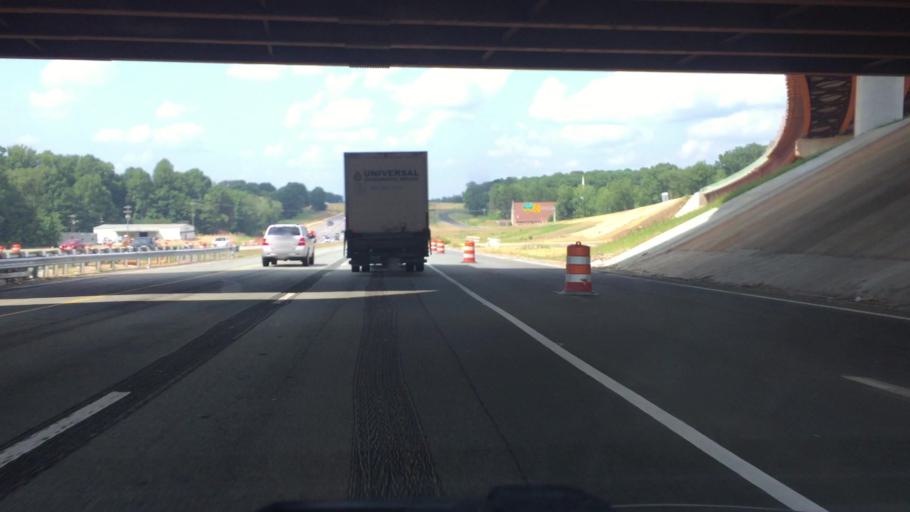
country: US
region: North Carolina
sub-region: Guilford County
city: McLeansville
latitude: 36.1431
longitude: -79.7350
